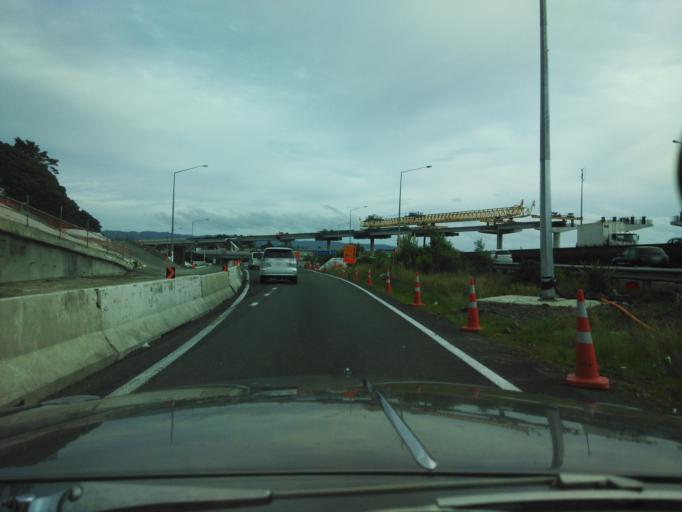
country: NZ
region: Auckland
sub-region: Auckland
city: Rosebank
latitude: -36.8719
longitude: 174.7075
